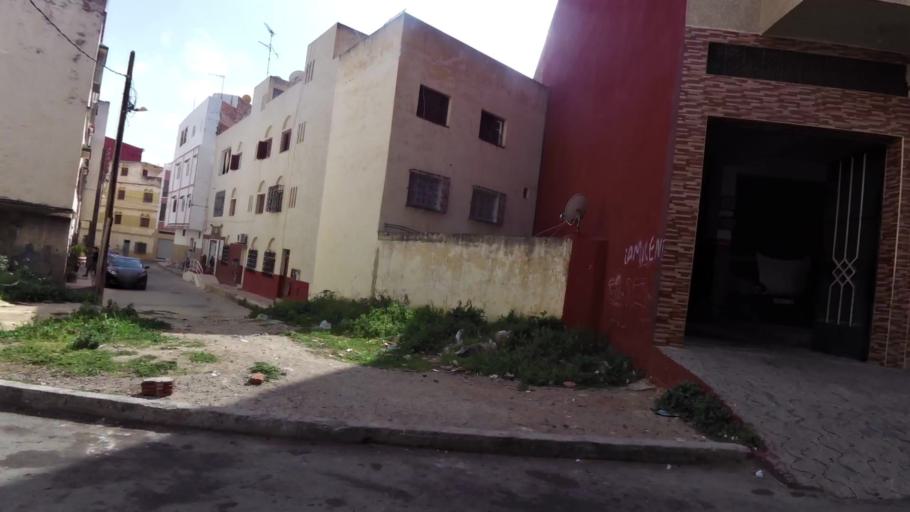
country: MA
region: Tanger-Tetouan
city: Tetouan
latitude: 35.5844
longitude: -5.3555
